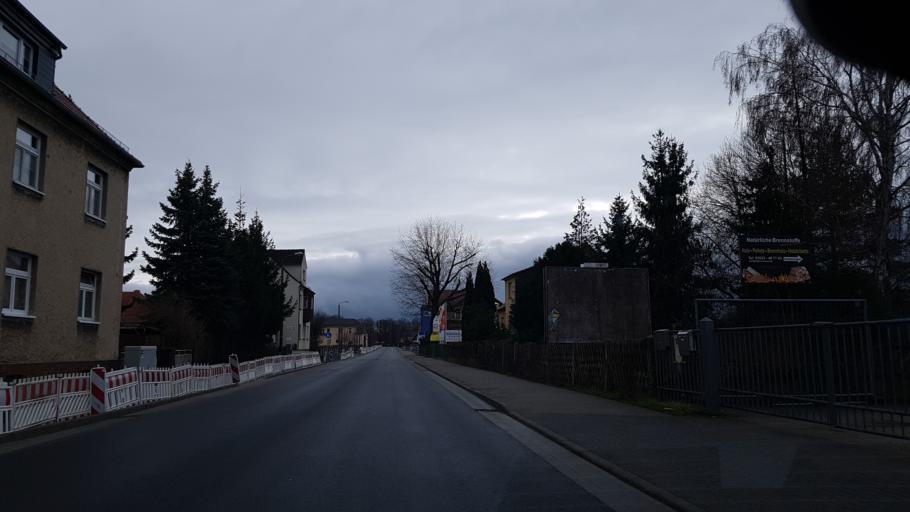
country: DE
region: Brandenburg
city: Elsterwerda
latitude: 51.4584
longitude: 13.5174
